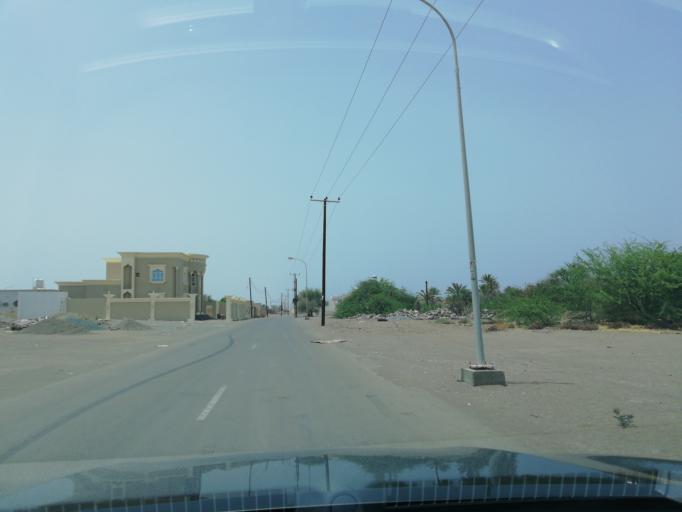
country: OM
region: Al Batinah
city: Al Liwa'
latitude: 24.6143
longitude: 56.5362
